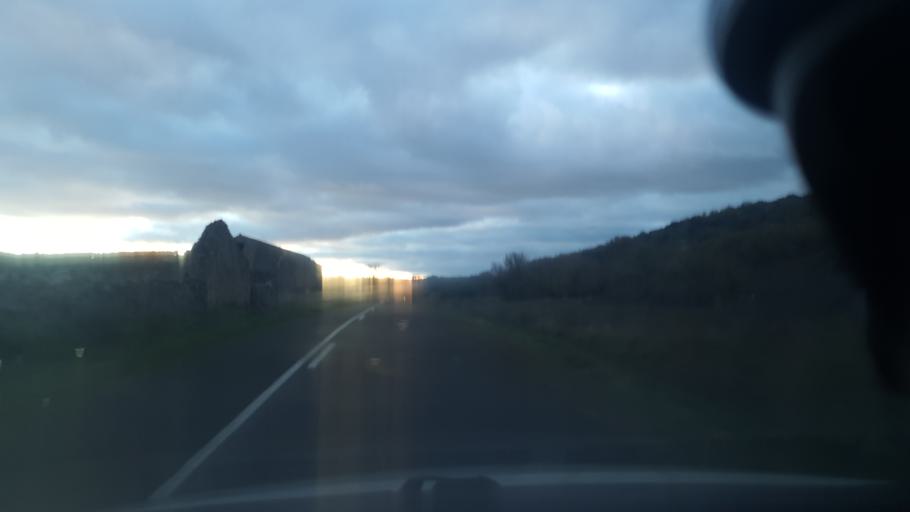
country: ES
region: Castille and Leon
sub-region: Provincia de Segovia
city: Vegas de Matute
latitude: 40.7137
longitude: -4.3114
